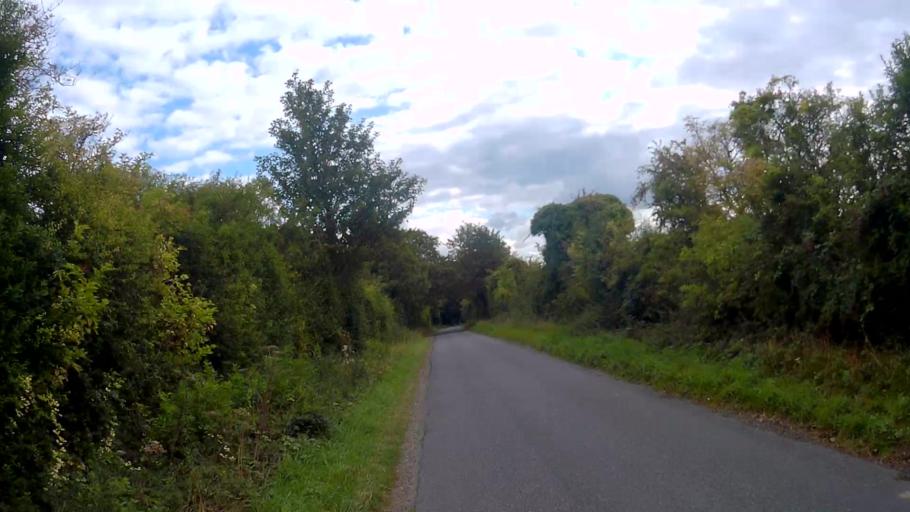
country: GB
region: England
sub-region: Hampshire
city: Kings Worthy
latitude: 51.1572
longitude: -1.3252
